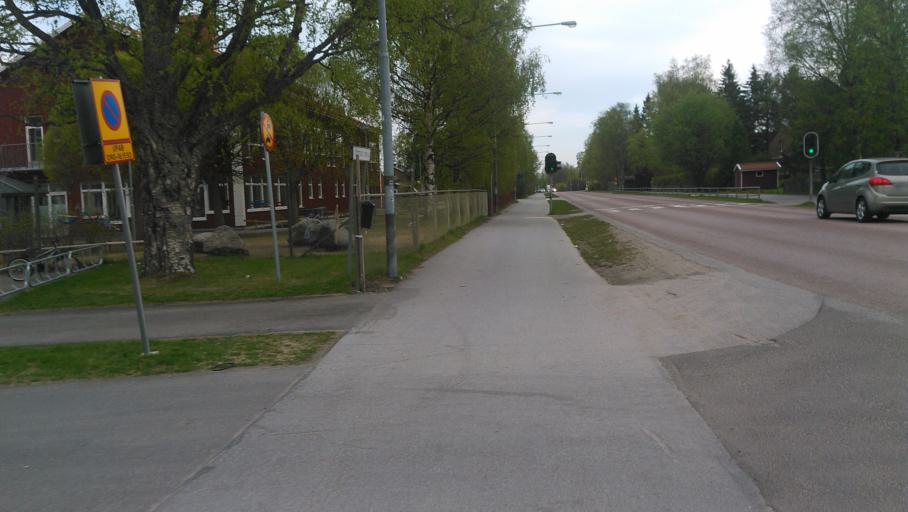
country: SE
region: Vaesterbotten
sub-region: Umea Kommun
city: Umea
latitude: 63.8131
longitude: 20.2666
